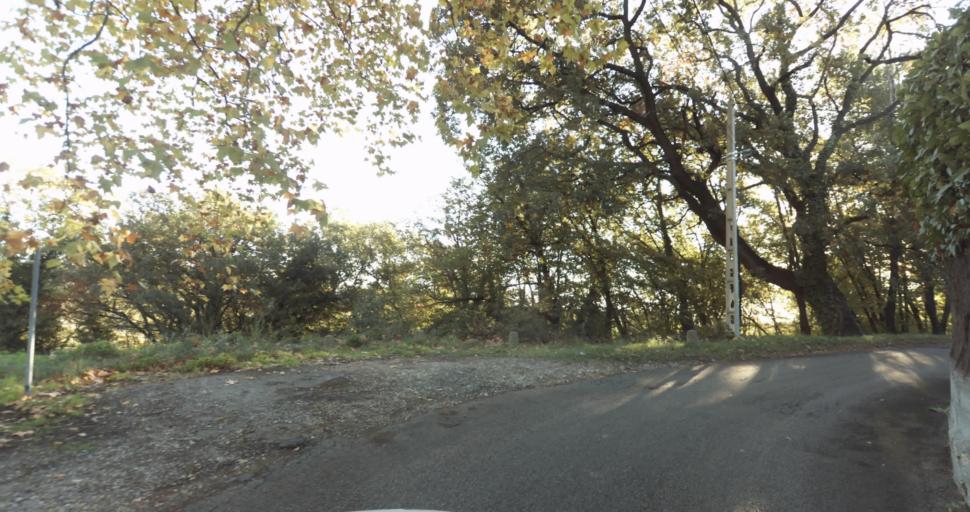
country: FR
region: Provence-Alpes-Cote d'Azur
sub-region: Departement des Alpes-Maritimes
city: Vence
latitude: 43.7240
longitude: 7.1222
